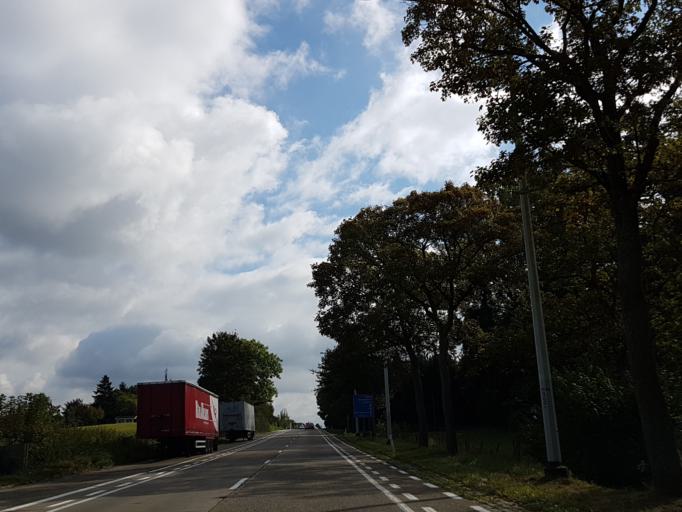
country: BE
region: Flanders
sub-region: Provincie Vlaams-Brabant
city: Boutersem
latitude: 50.8488
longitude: 4.8160
